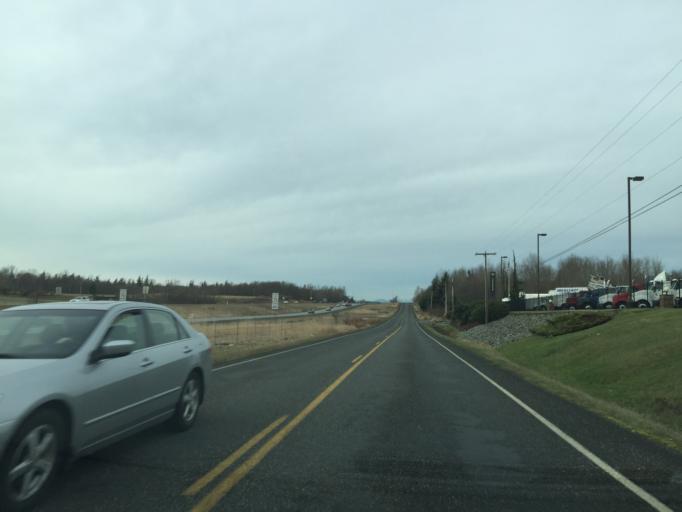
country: US
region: Washington
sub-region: Whatcom County
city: Marietta-Alderwood
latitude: 48.8027
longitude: -122.5333
